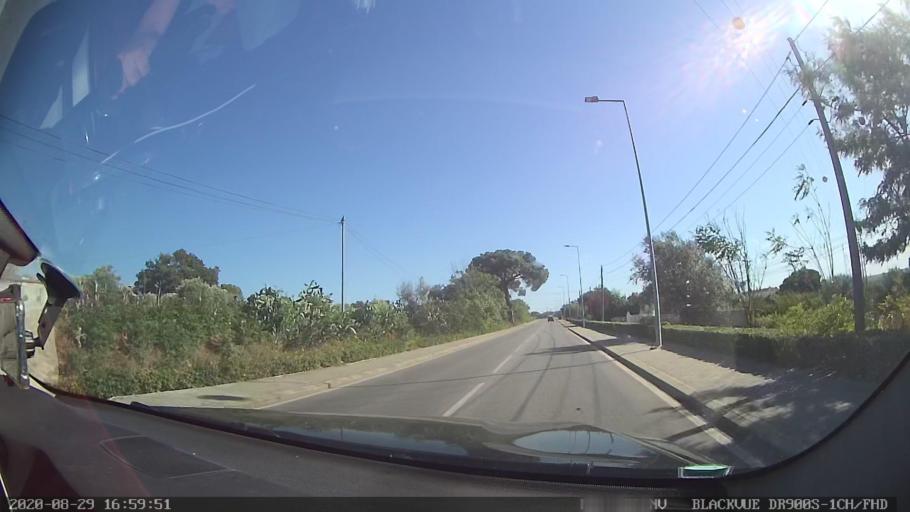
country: PT
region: Setubal
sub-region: Alcacer do Sal
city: Alcacer do Sal
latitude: 38.3842
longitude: -8.5132
